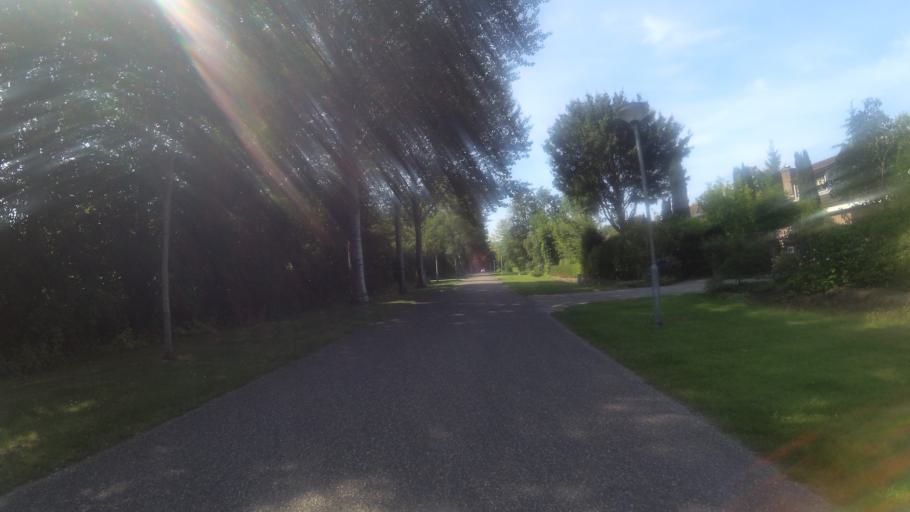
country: NL
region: Zeeland
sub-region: Gemeente Noord-Beveland
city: Kamperland
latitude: 51.5720
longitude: 3.7098
